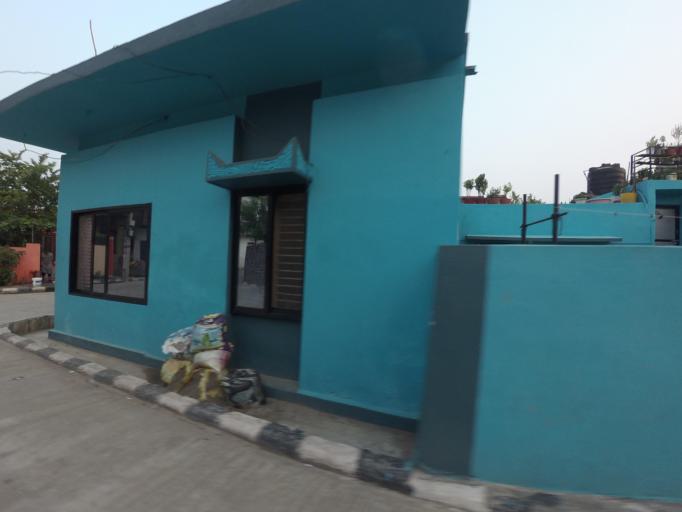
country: NP
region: Western Region
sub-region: Lumbini Zone
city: Bhairahawa
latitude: 27.5042
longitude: 83.4609
